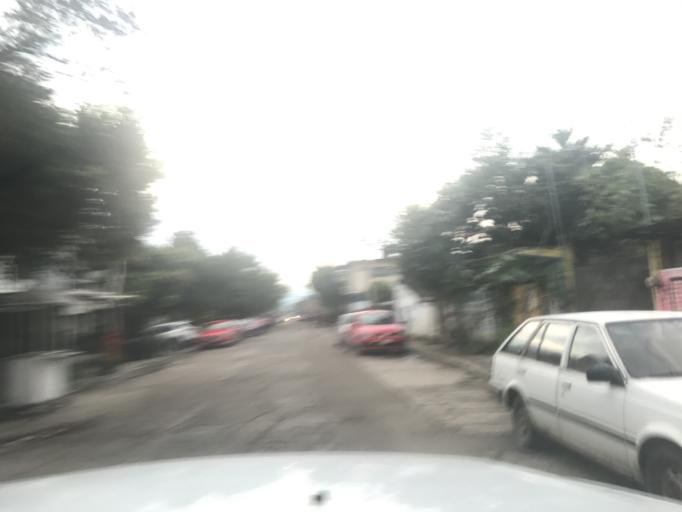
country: MX
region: Morelos
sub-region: Jojutla
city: Jojutla
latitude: 18.6122
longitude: -99.1721
